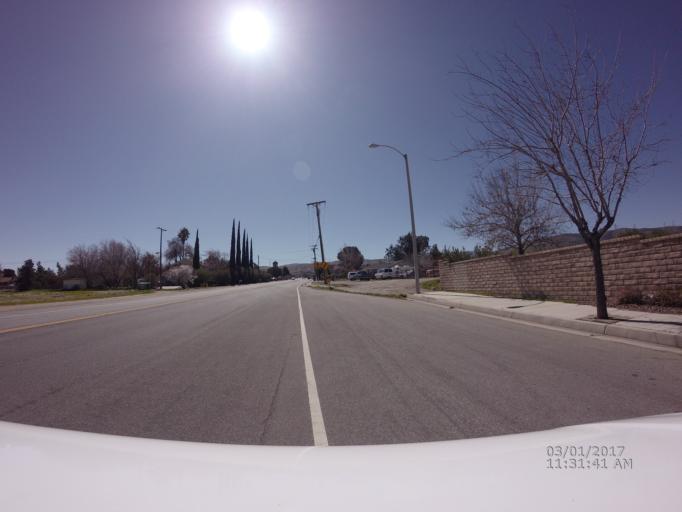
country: US
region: California
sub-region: Los Angeles County
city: Quartz Hill
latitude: 34.6333
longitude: -118.2189
